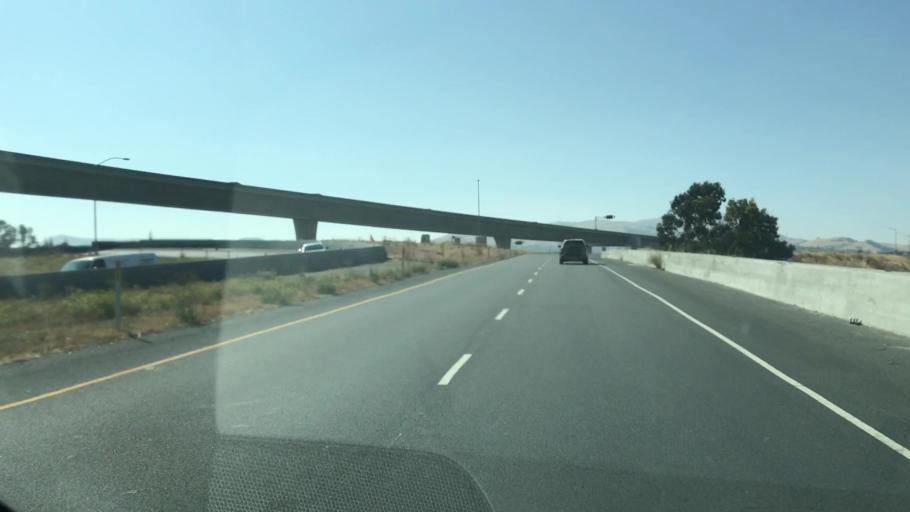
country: US
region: California
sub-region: Alameda County
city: Dublin
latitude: 37.7021
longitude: -121.9214
